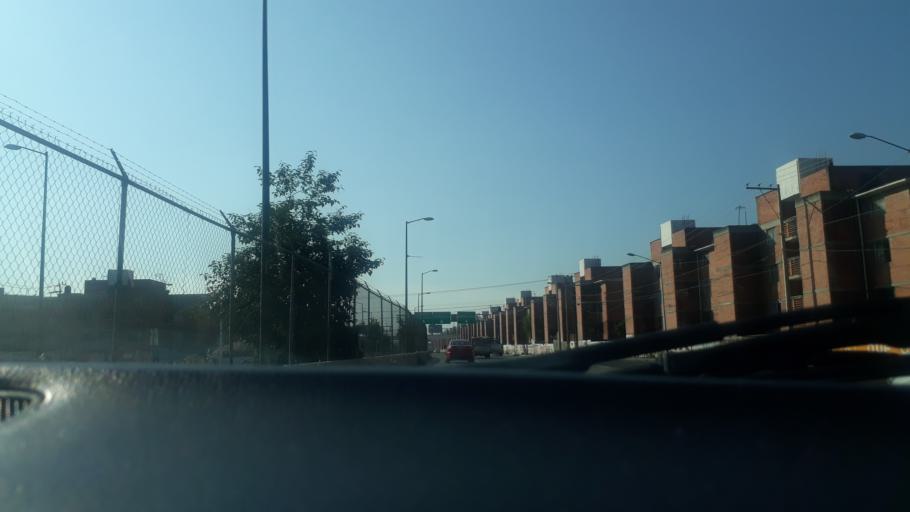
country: MX
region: Puebla
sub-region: Puebla
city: El Capulo (La Quebradora)
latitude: 18.9890
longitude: -98.2395
